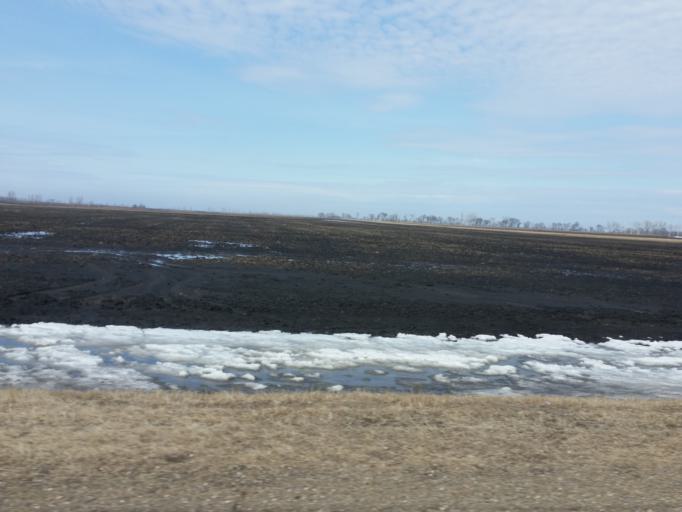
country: US
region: North Dakota
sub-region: Walsh County
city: Grafton
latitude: 48.4265
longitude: -97.2357
